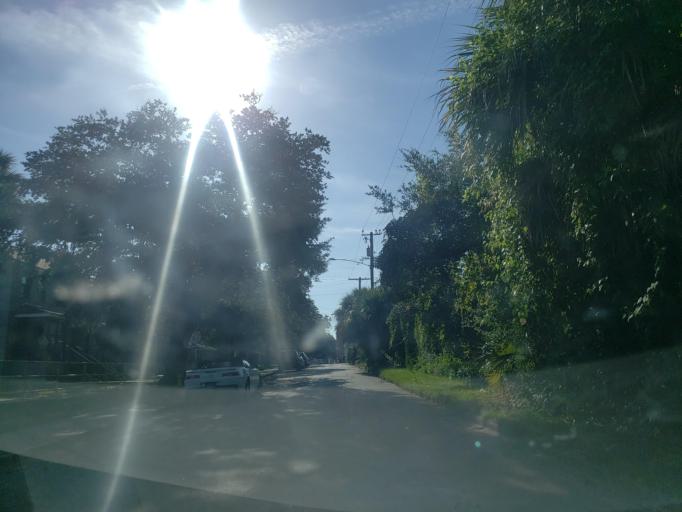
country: US
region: Georgia
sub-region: Chatham County
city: Savannah
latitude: 32.0811
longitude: -81.1012
